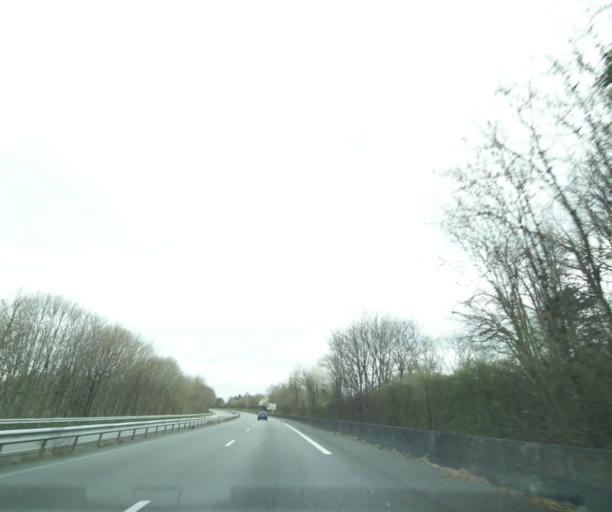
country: FR
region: Limousin
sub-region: Departement de la Haute-Vienne
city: Saint-Germain-les-Belles
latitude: 45.5978
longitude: 1.4491
